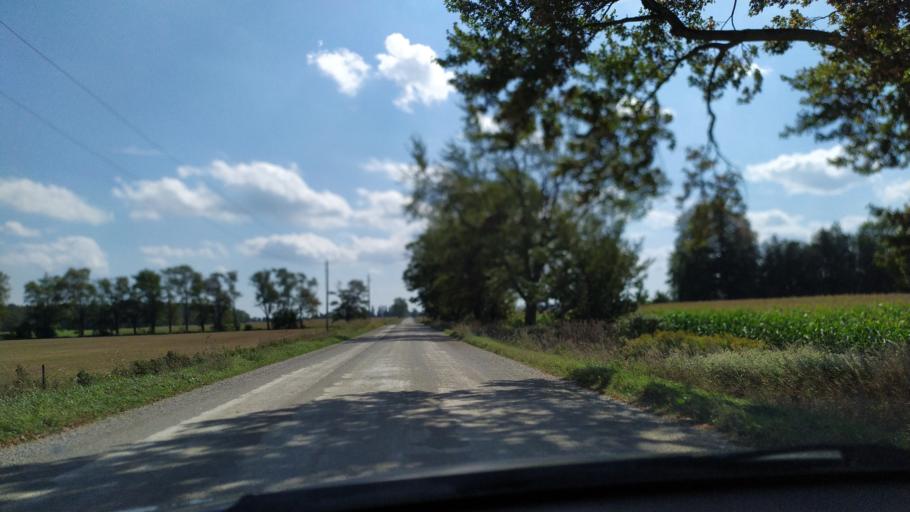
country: CA
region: Ontario
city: Stratford
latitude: 43.2823
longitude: -80.9273
